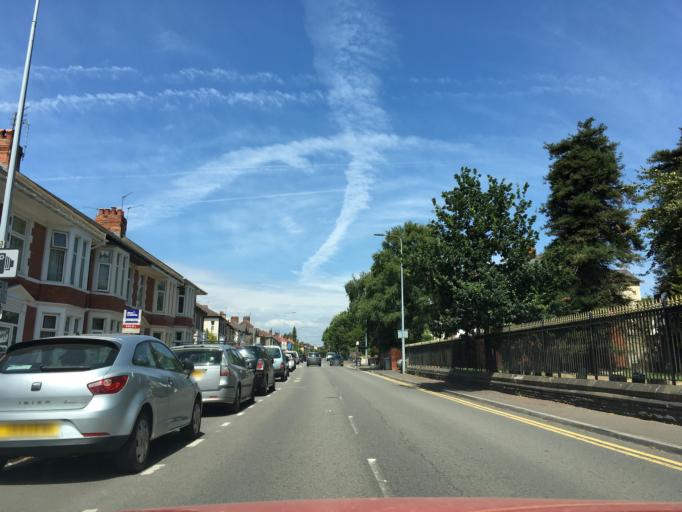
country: GB
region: Wales
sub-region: Cardiff
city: Cardiff
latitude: 51.5077
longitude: -3.1829
